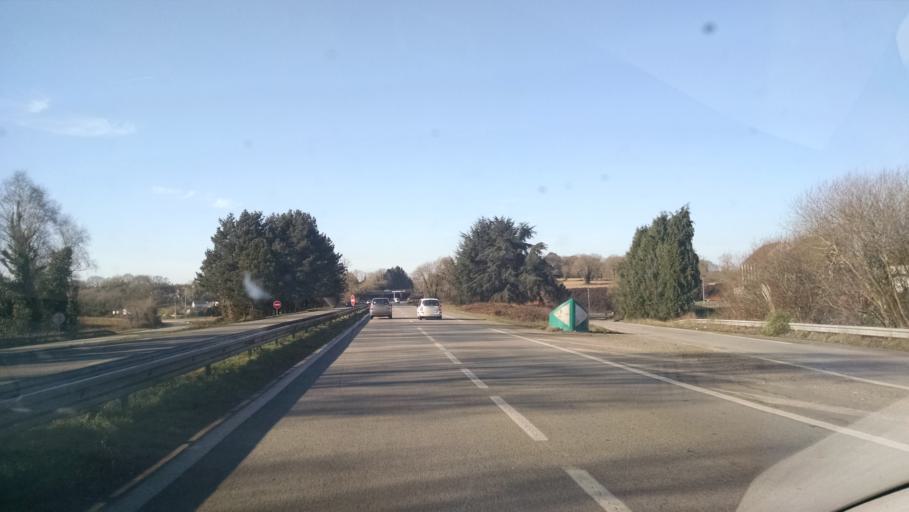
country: FR
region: Brittany
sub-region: Departement du Morbihan
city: Hennebont
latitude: 47.7890
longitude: -3.2728
